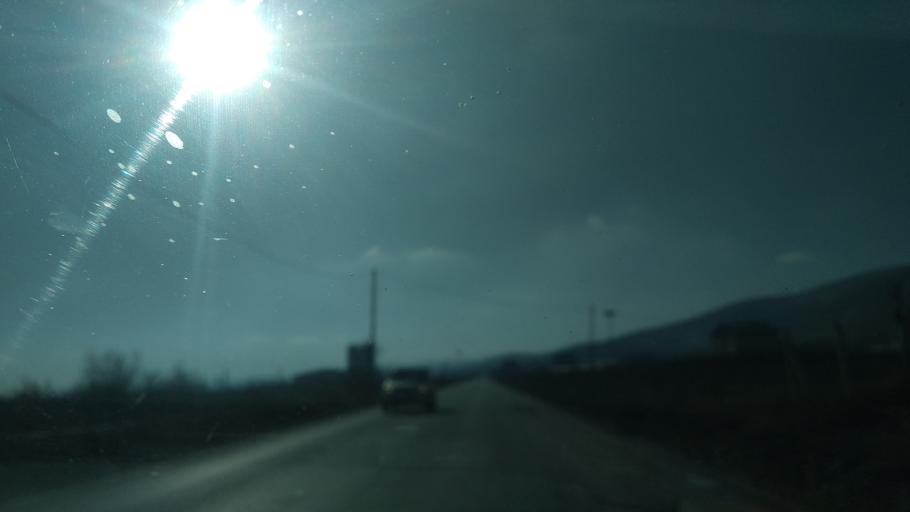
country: XK
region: Pristina
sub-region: Komuna e Gracanices
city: Glanica
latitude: 42.5845
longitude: 21.0161
